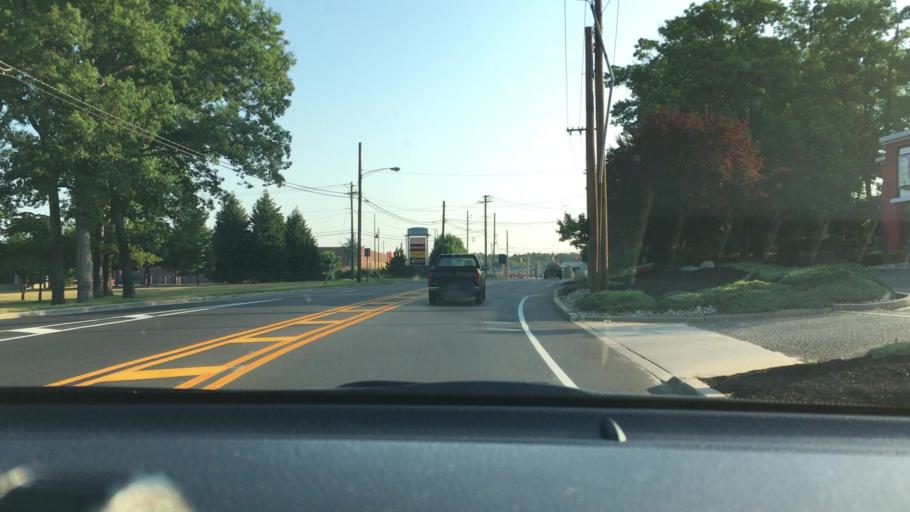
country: US
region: New Jersey
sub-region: Cumberland County
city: Millville
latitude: 39.4180
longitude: -75.0402
